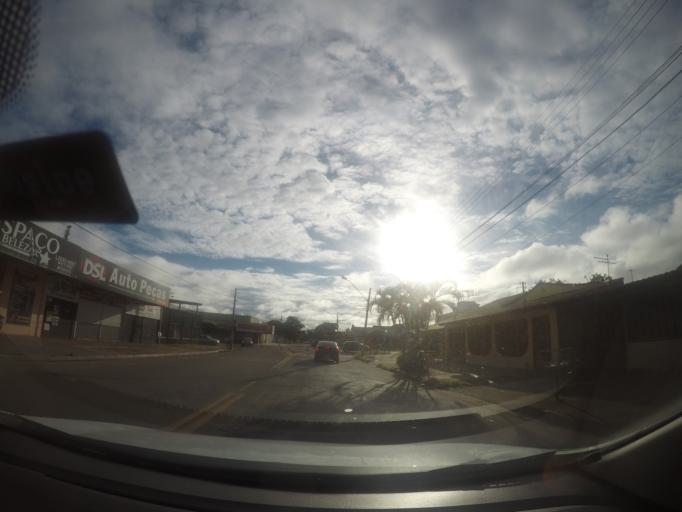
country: BR
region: Goias
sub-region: Goiania
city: Goiania
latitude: -16.6873
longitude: -49.3118
